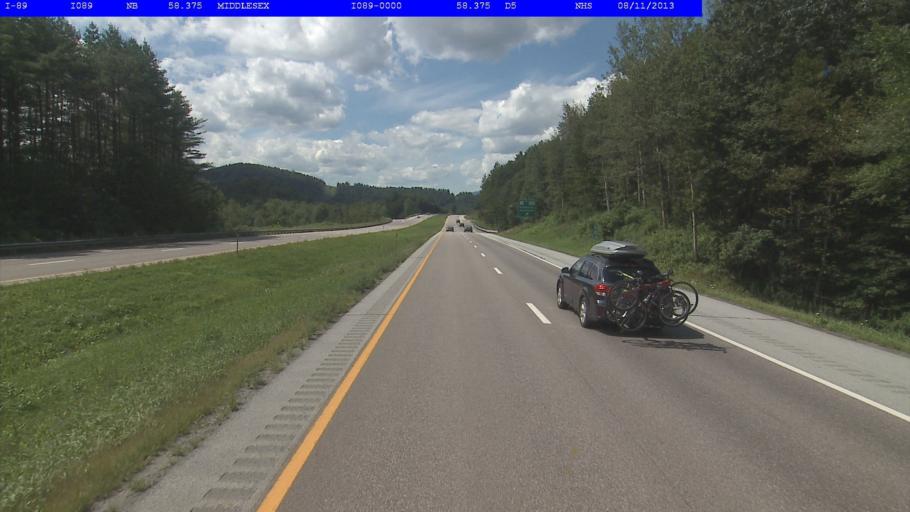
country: US
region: Vermont
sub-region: Washington County
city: Waterbury
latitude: 44.2952
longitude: -72.6799
